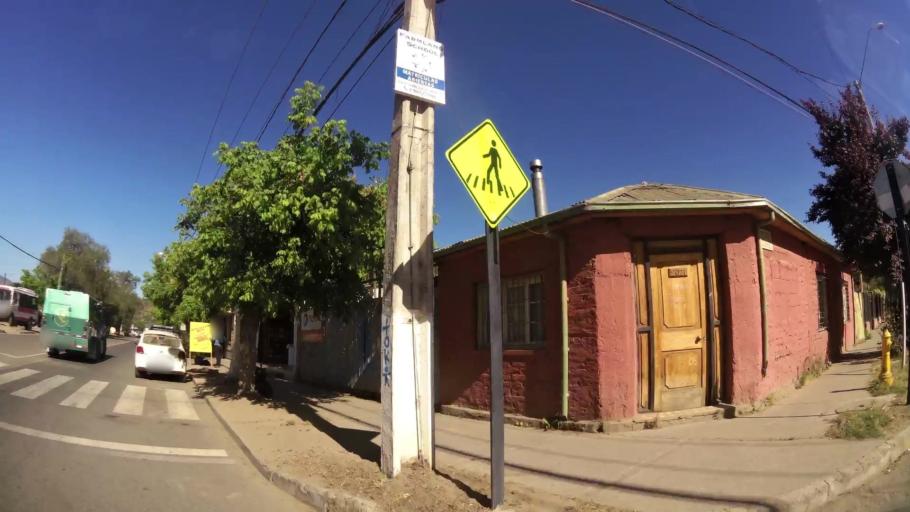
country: CL
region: Santiago Metropolitan
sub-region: Provincia de Chacabuco
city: Lampa
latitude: -33.4024
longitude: -71.1268
